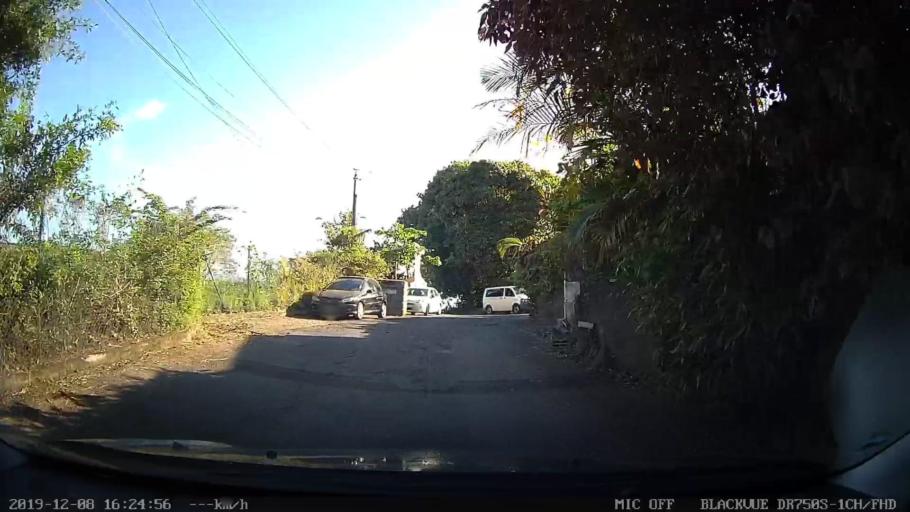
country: RE
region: Reunion
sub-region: Reunion
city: Sainte-Marie
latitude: -20.9261
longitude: 55.5314
